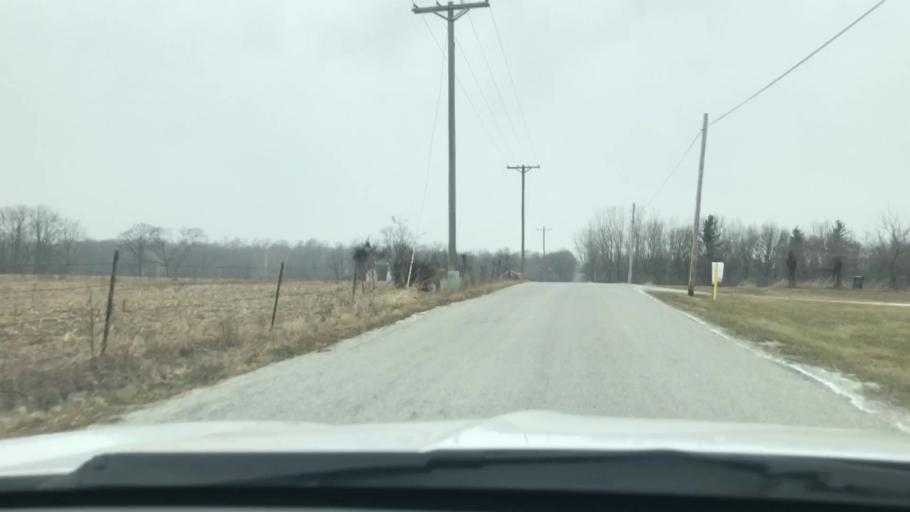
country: US
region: Indiana
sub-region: Fulton County
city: Akron
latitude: 41.0406
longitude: -86.0570
